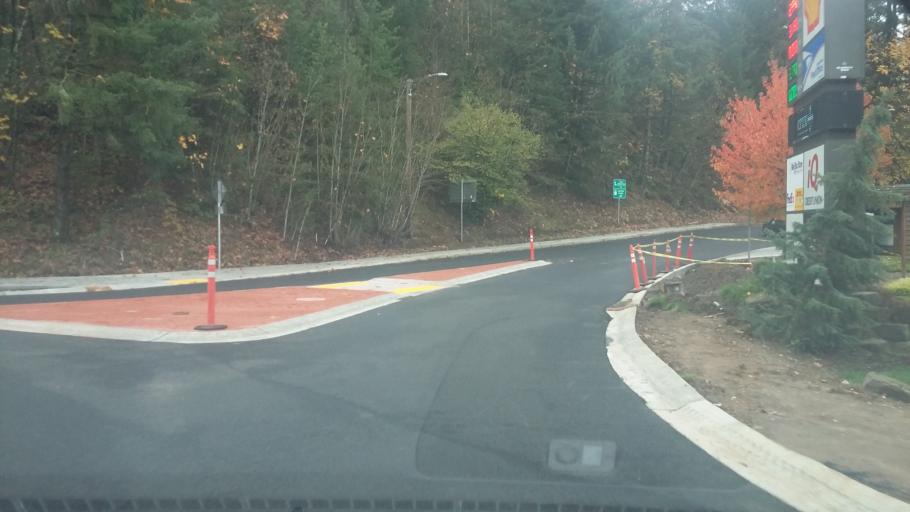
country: US
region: Washington
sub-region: Clark County
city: Camas
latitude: 45.5821
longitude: -122.4270
